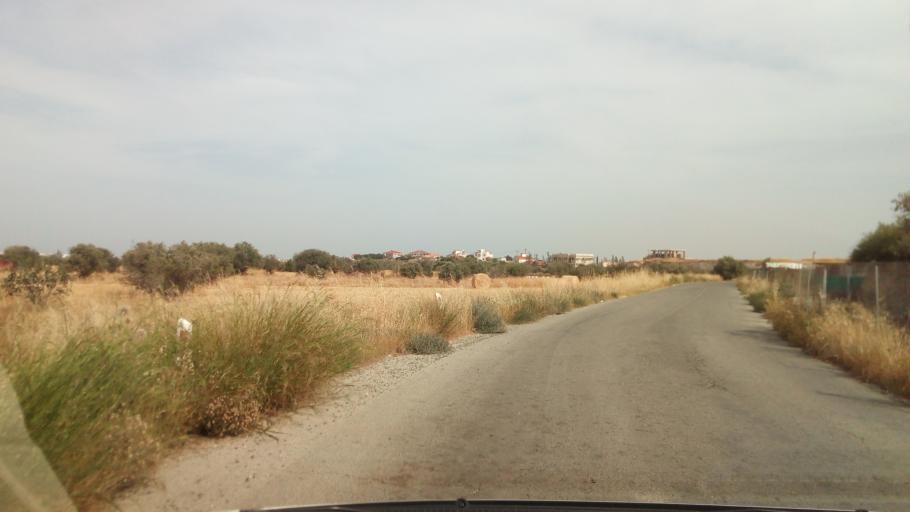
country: CY
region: Larnaka
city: Livadia
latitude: 34.9535
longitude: 33.6113
